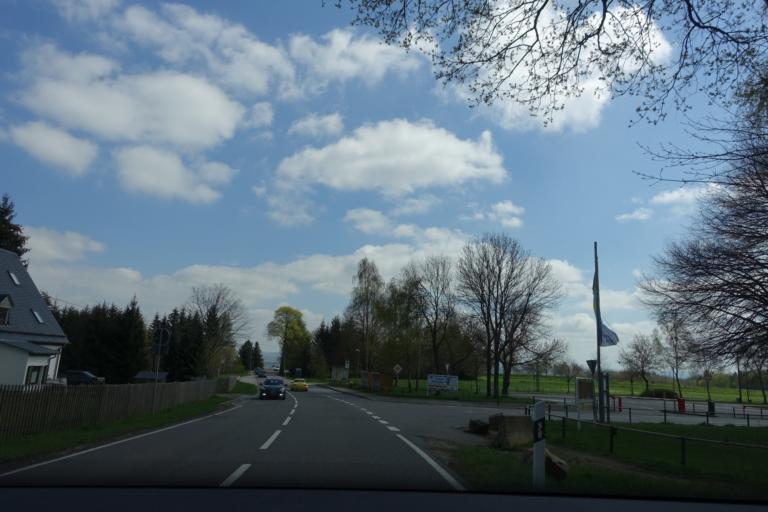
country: DE
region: Saxony
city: Limbach-Oberfrohna
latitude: 50.8414
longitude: 12.8139
